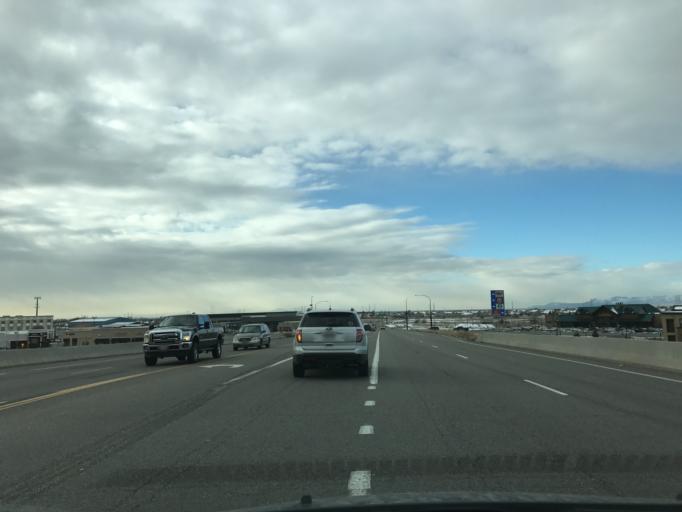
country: US
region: Utah
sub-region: Davis County
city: Farmington
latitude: 40.9882
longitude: -111.9073
